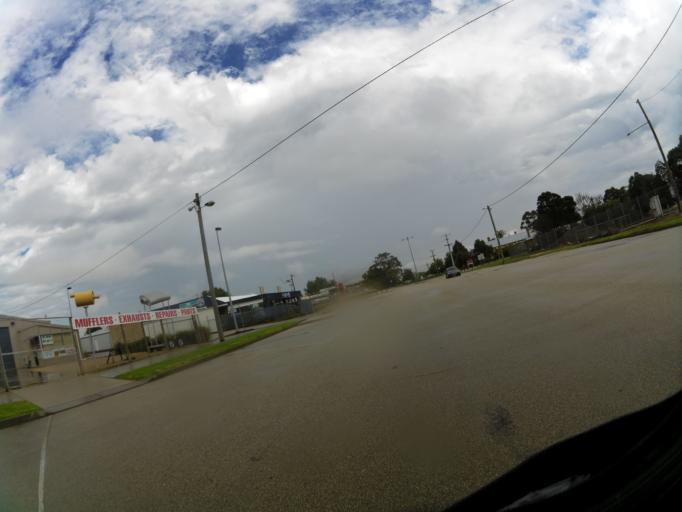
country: AU
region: Victoria
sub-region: East Gippsland
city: Bairnsdale
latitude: -37.8279
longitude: 147.6300
